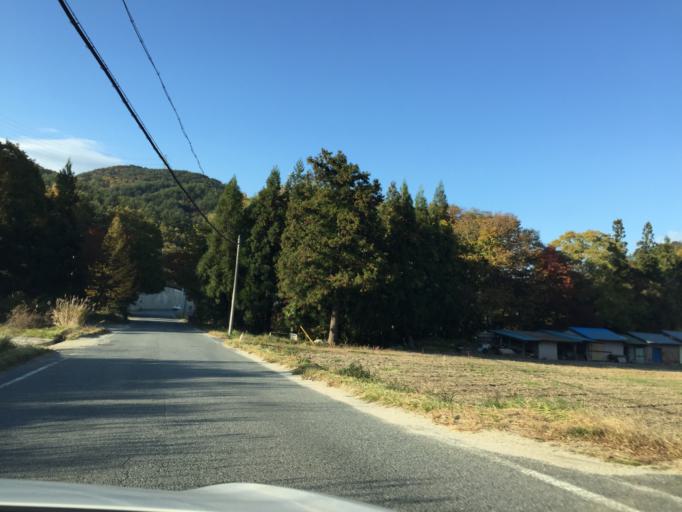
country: JP
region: Fukushima
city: Funehikimachi-funehiki
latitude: 37.2899
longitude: 140.7589
